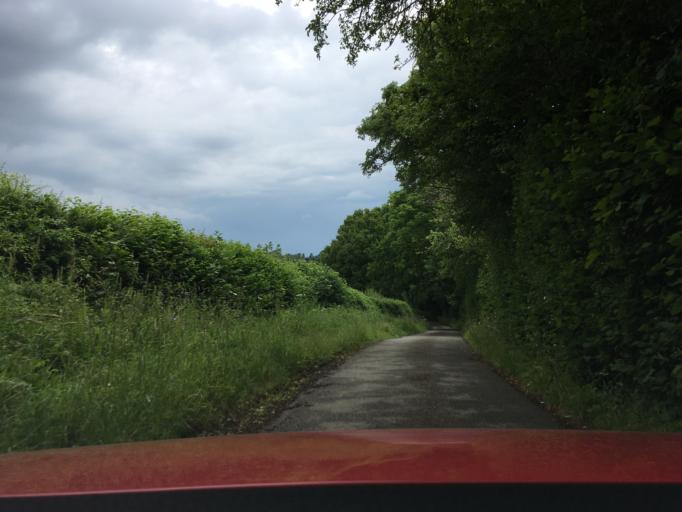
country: GB
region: England
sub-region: Gloucestershire
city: Shurdington
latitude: 51.8032
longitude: -2.0832
